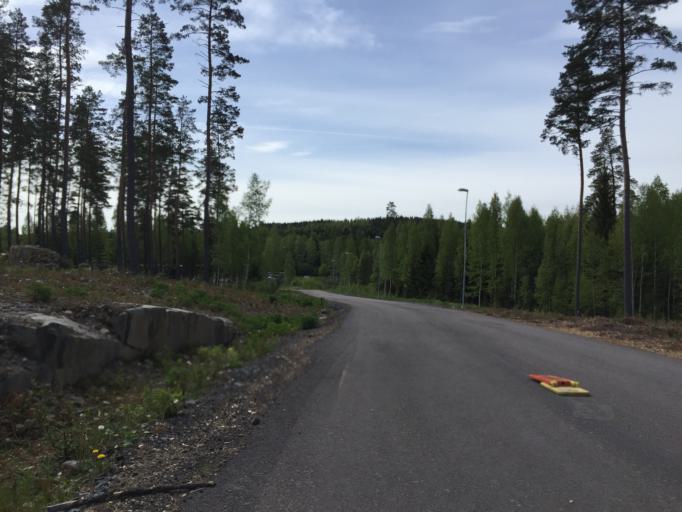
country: SE
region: Dalarna
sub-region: Ludvika Kommun
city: Ludvika
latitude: 60.1377
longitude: 15.1530
